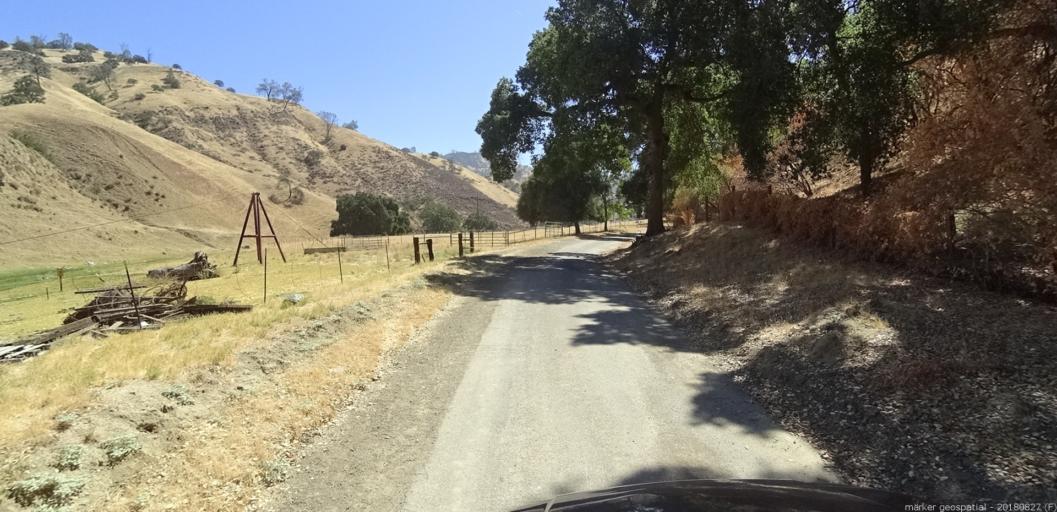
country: US
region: California
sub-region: Monterey County
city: King City
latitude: 36.2818
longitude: -120.8492
